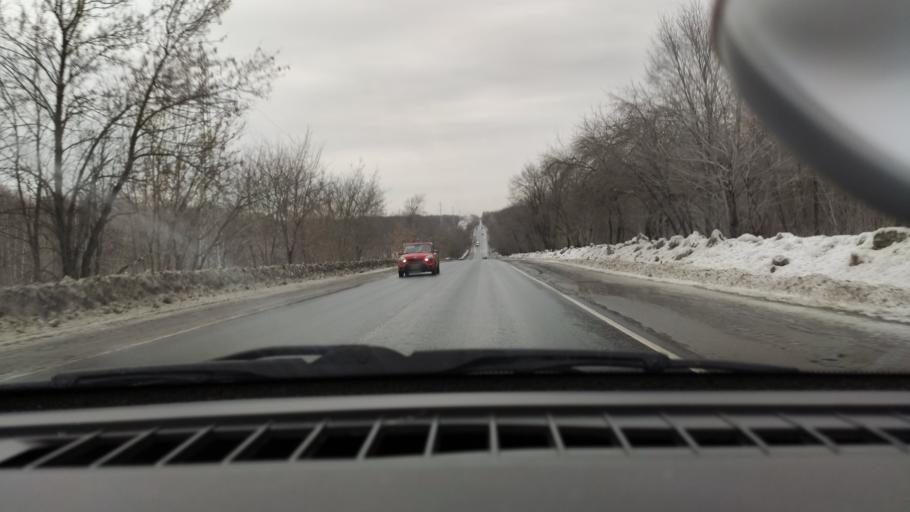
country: RU
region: Samara
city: Novosemeykino
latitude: 53.3233
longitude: 50.2639
